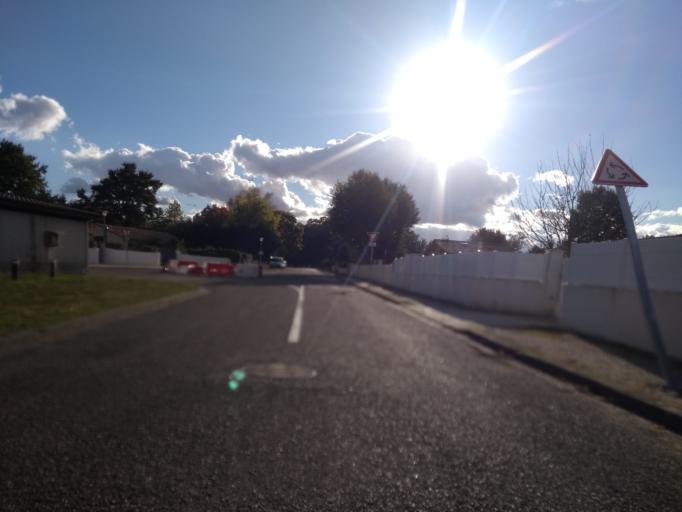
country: FR
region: Aquitaine
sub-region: Departement de la Gironde
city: Cestas
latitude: 44.7174
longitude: -0.6890
